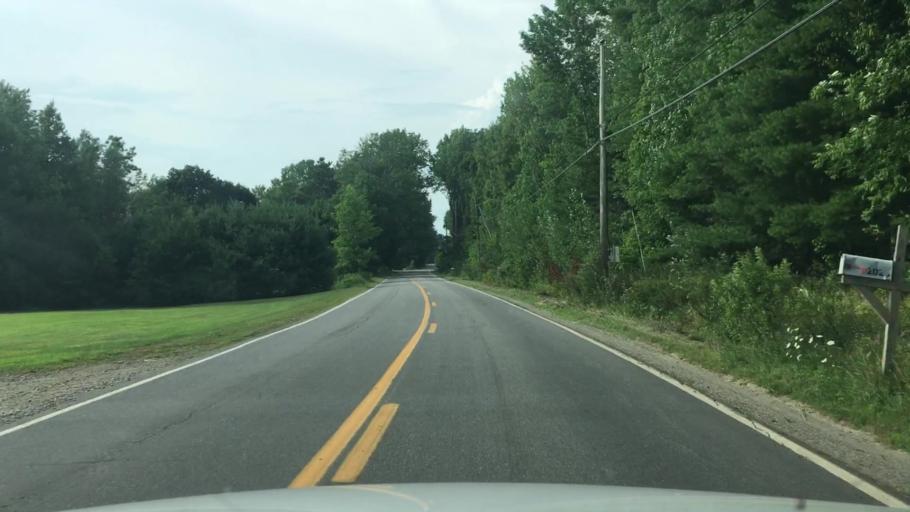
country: US
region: Maine
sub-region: Lincoln County
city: Waldoboro
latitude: 44.1568
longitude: -69.3760
